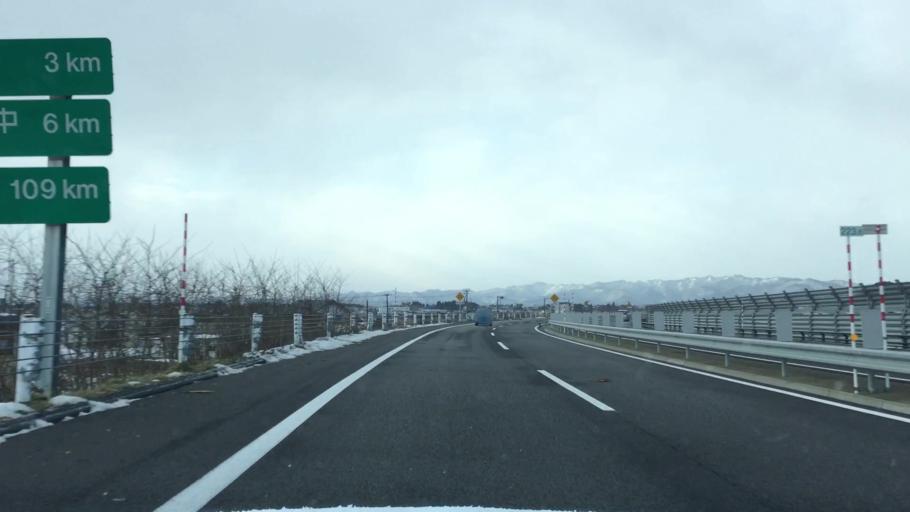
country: JP
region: Akita
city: Odate
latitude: 40.2939
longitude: 140.5527
